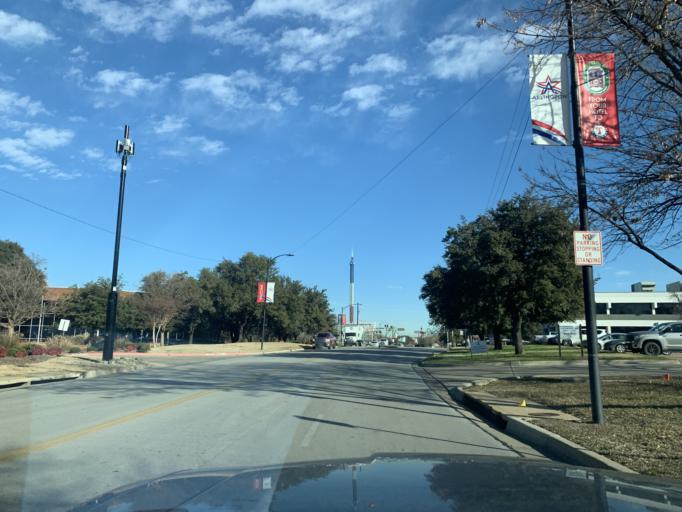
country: US
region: Texas
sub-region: Tarrant County
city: Arlington
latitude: 32.7510
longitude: -97.0687
